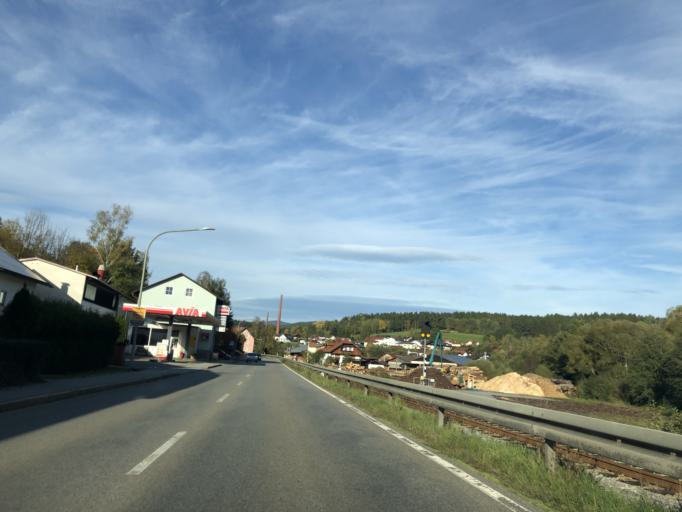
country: DE
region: Bavaria
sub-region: Lower Bavaria
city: Teisnach
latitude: 49.0336
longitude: 12.9932
